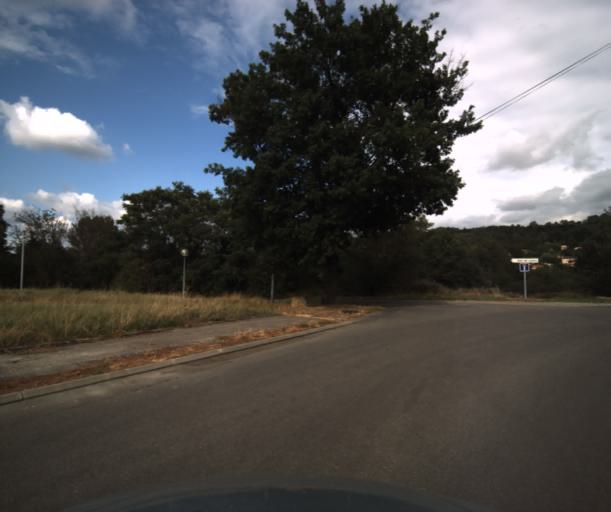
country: FR
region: Midi-Pyrenees
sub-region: Departement de la Haute-Garonne
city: Muret
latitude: 43.4461
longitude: 1.3247
